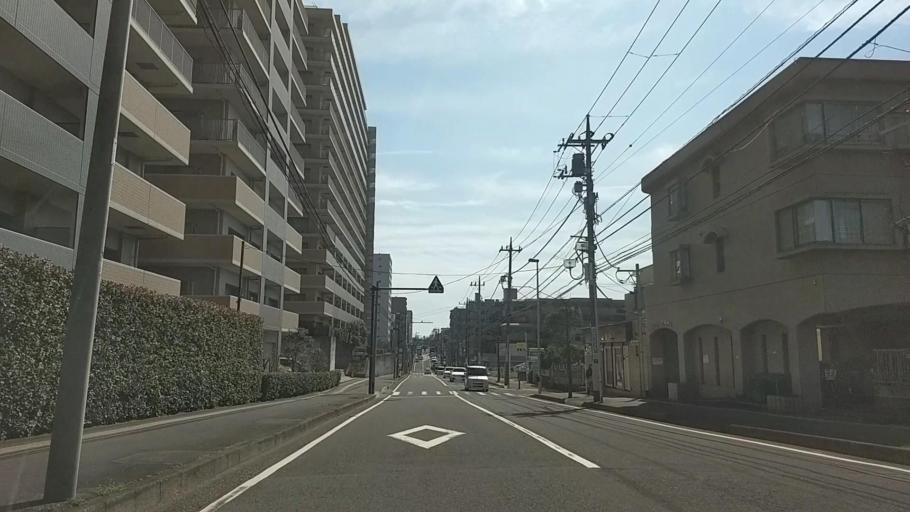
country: JP
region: Kanagawa
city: Fujisawa
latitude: 35.3990
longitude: 139.4623
